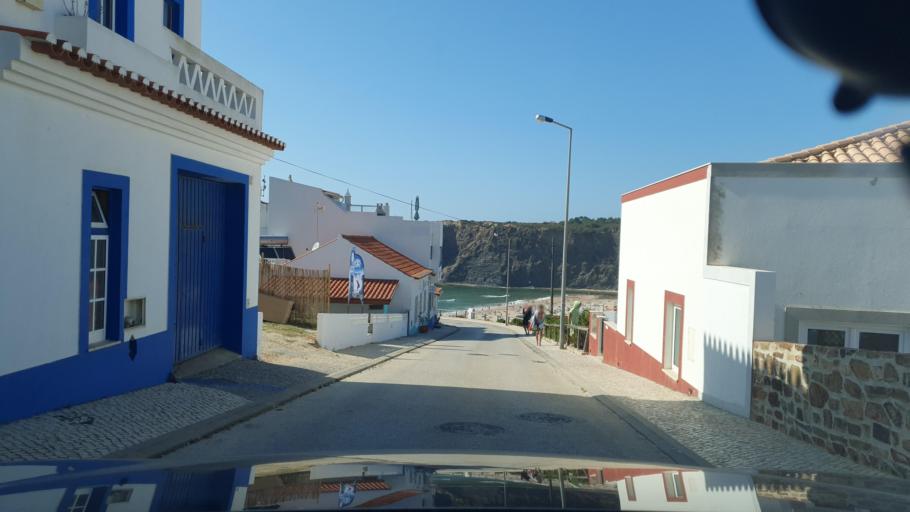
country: PT
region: Beja
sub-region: Odemira
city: Sao Teotonio
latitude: 37.4399
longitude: -8.7974
